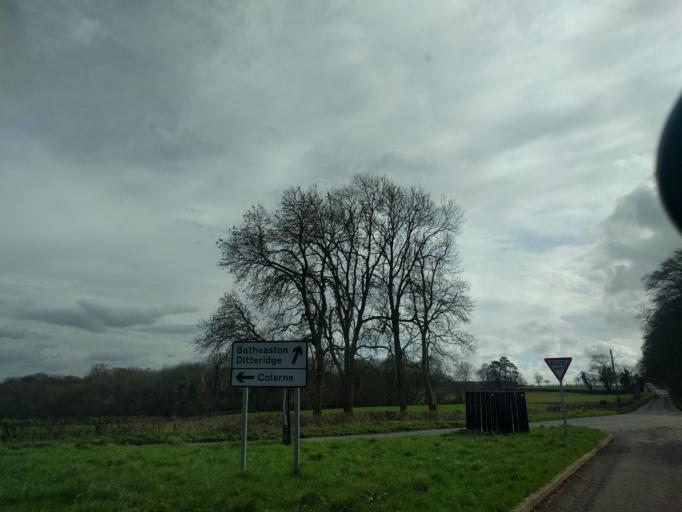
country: GB
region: England
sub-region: Wiltshire
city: Colerne
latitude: 51.4350
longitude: -2.2925
